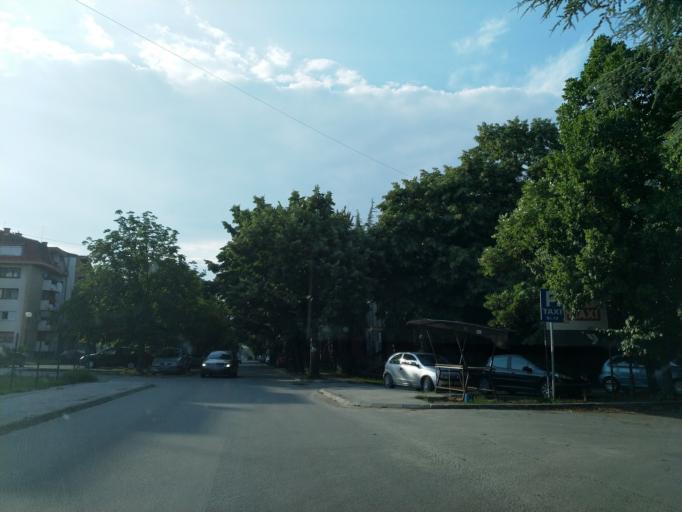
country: RS
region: Central Serbia
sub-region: Pomoravski Okrug
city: Jagodina
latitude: 43.9780
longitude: 21.2484
